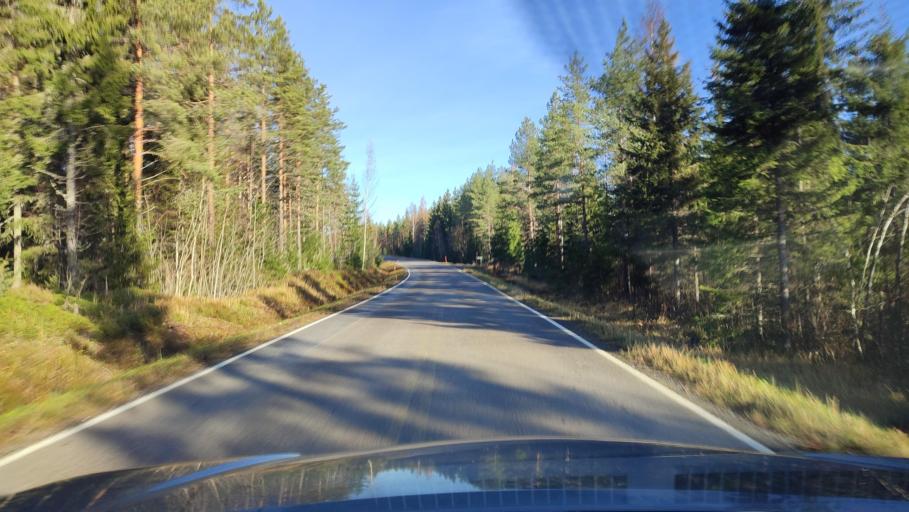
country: FI
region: Southern Ostrobothnia
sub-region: Suupohja
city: Karijoki
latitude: 62.3820
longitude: 21.6963
